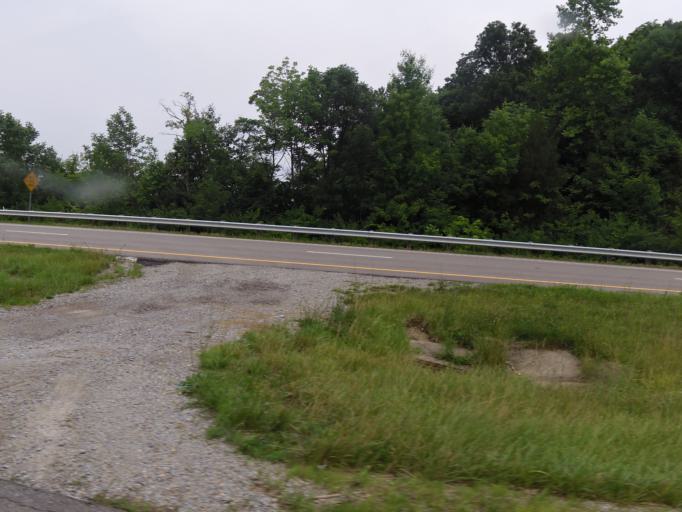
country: US
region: Ohio
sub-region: Warren County
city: Waynesville
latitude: 39.5060
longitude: -84.0230
